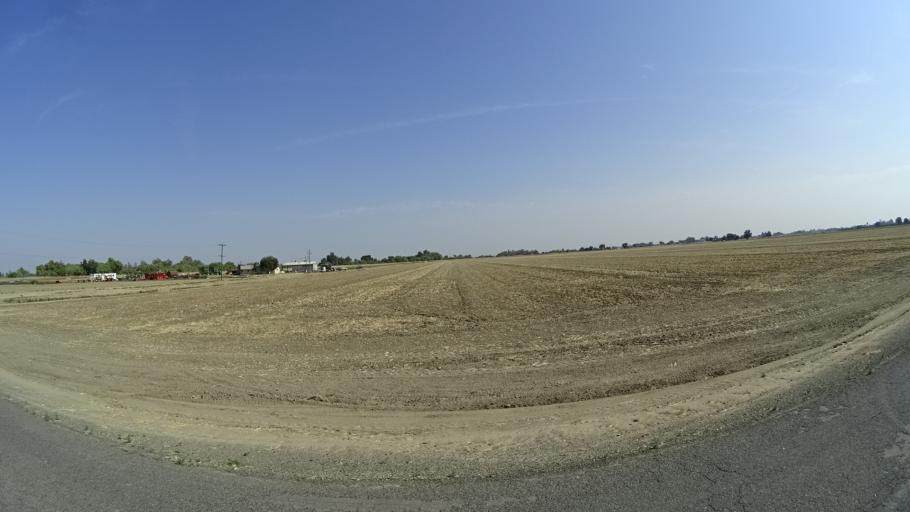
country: US
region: California
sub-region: Kings County
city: Lemoore Station
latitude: 36.3283
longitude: -119.8731
